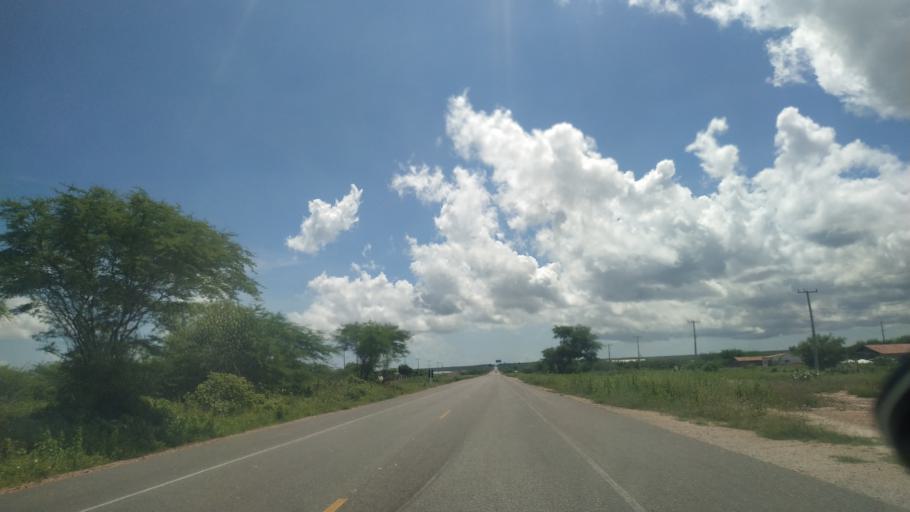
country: BR
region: Rio Grande do Norte
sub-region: Areia Branca
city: Areia Branca
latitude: -5.0571
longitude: -37.1554
